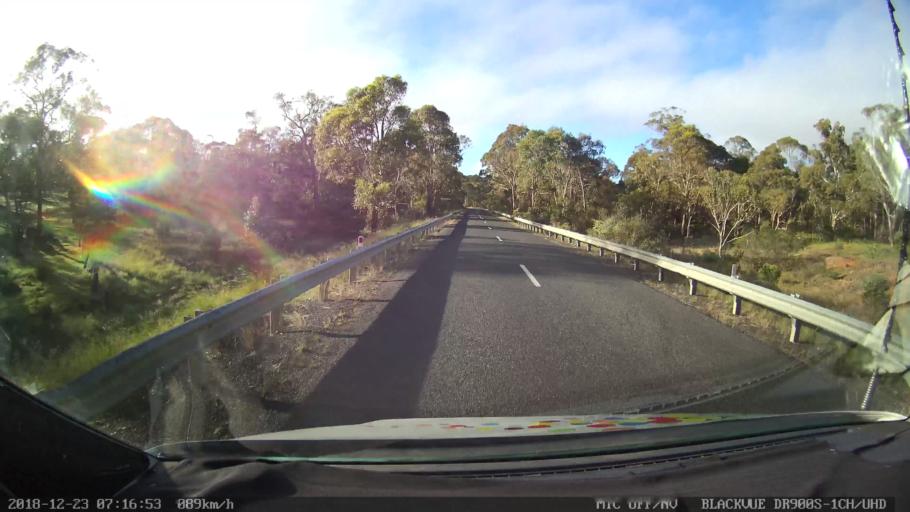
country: AU
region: New South Wales
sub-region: Bellingen
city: Dorrigo
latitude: -30.4615
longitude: 152.3077
